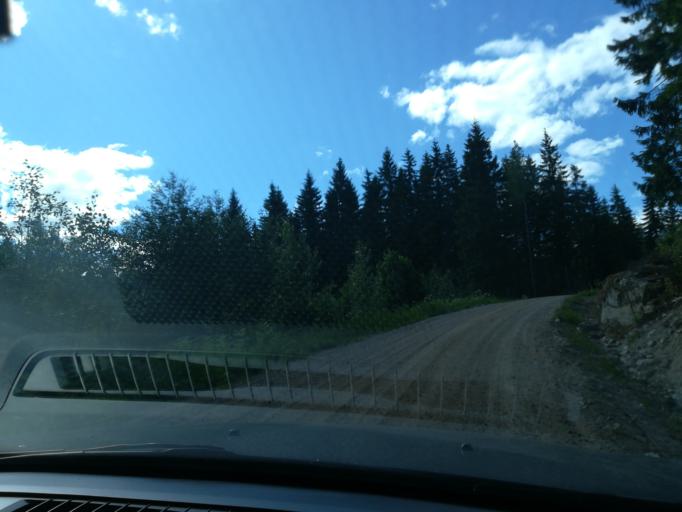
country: FI
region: Southern Savonia
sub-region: Mikkeli
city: Puumala
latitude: 61.6496
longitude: 28.1786
